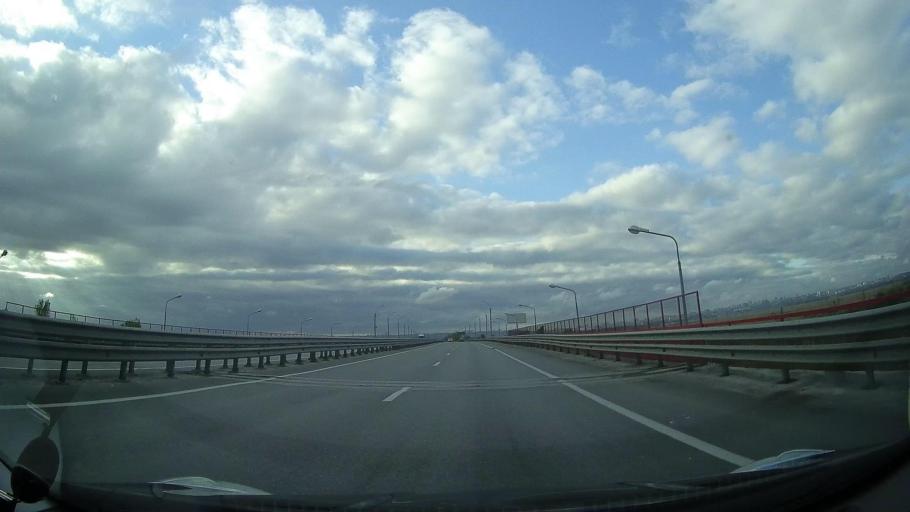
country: RU
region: Rostov
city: Bataysk
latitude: 47.1644
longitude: 39.7588
